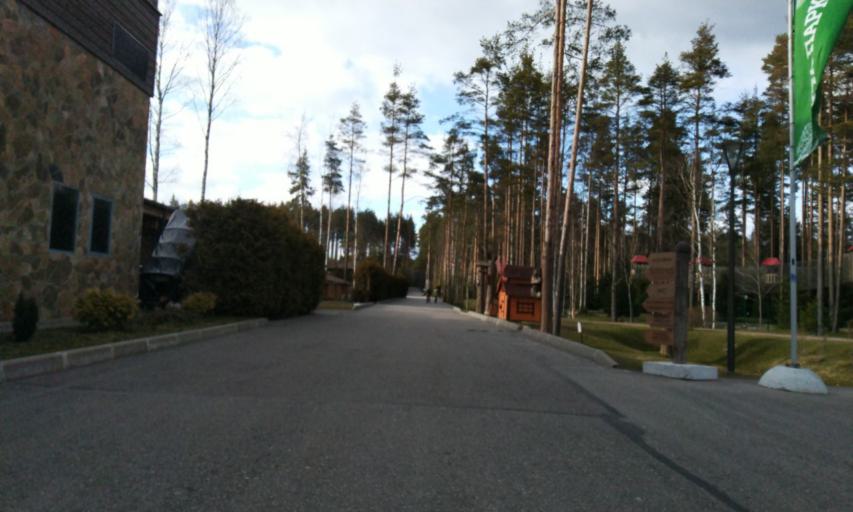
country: RU
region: Leningrad
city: Novoye Devyatkino
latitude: 60.1280
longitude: 30.4459
